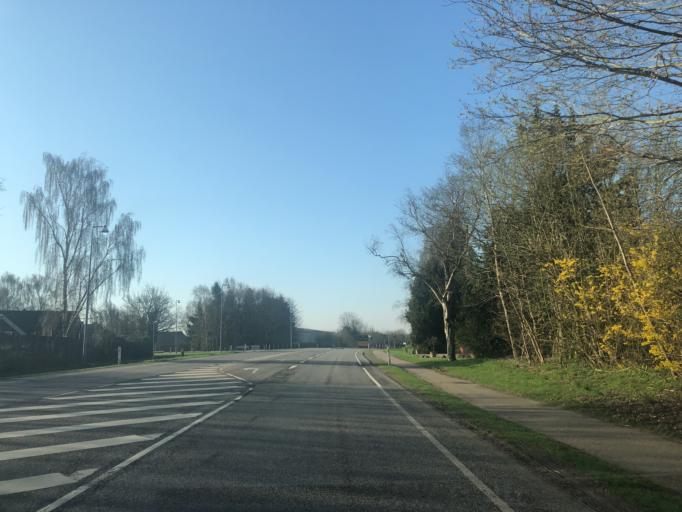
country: DK
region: Zealand
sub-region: Faxe Kommune
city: Haslev
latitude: 55.3382
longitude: 11.9433
